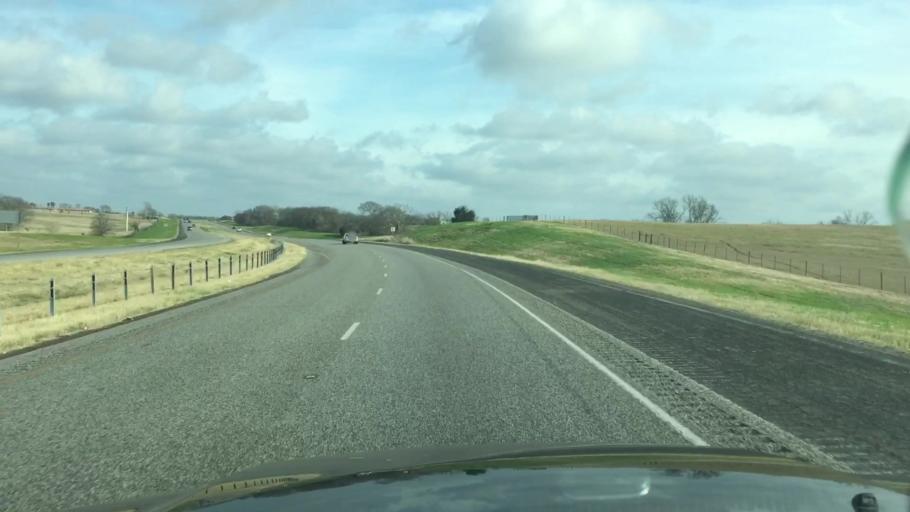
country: US
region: Texas
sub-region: Washington County
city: Brenham
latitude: 30.1377
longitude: -96.3501
